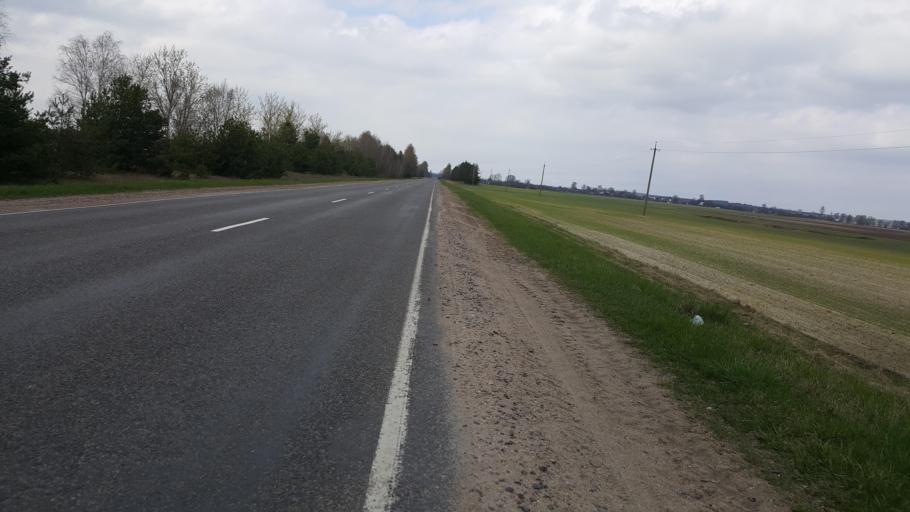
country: BY
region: Brest
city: Kamyanyets
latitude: 52.3466
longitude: 23.9029
